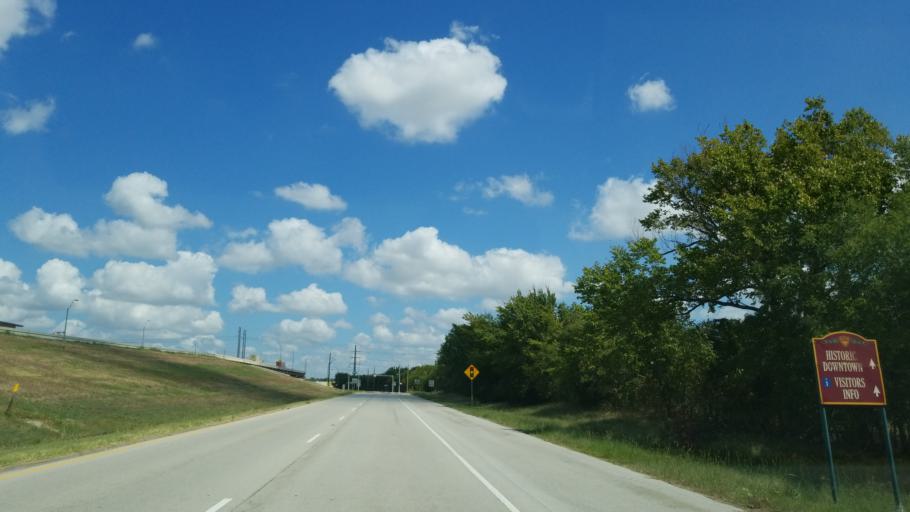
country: US
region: Texas
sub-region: Tarrant County
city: Grapevine
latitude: 32.9180
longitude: -97.0911
